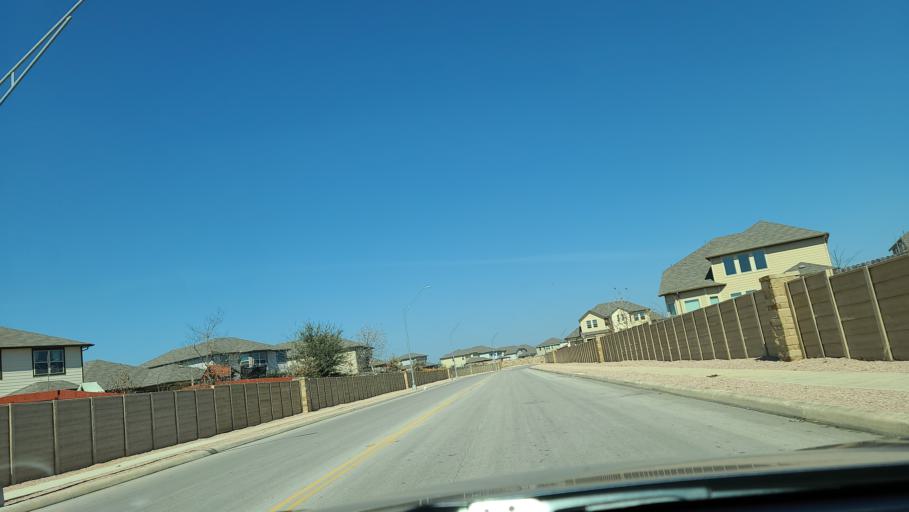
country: US
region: Texas
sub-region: Bexar County
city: Leon Valley
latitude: 29.5598
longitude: -98.6205
